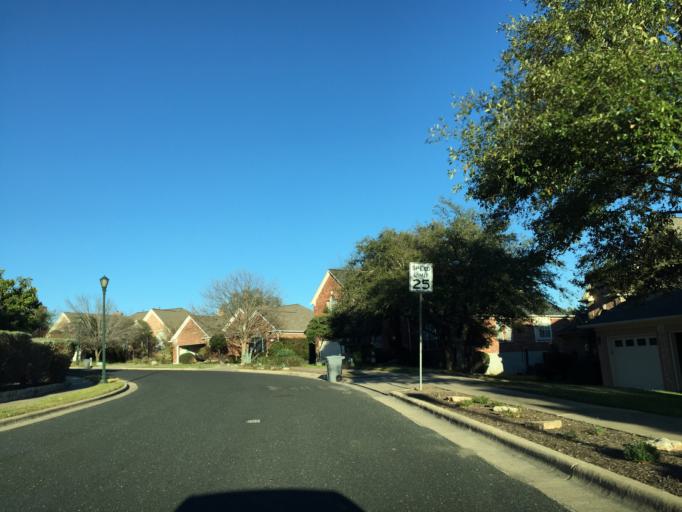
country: US
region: Texas
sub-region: Williamson County
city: Jollyville
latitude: 30.4298
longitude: -97.7866
